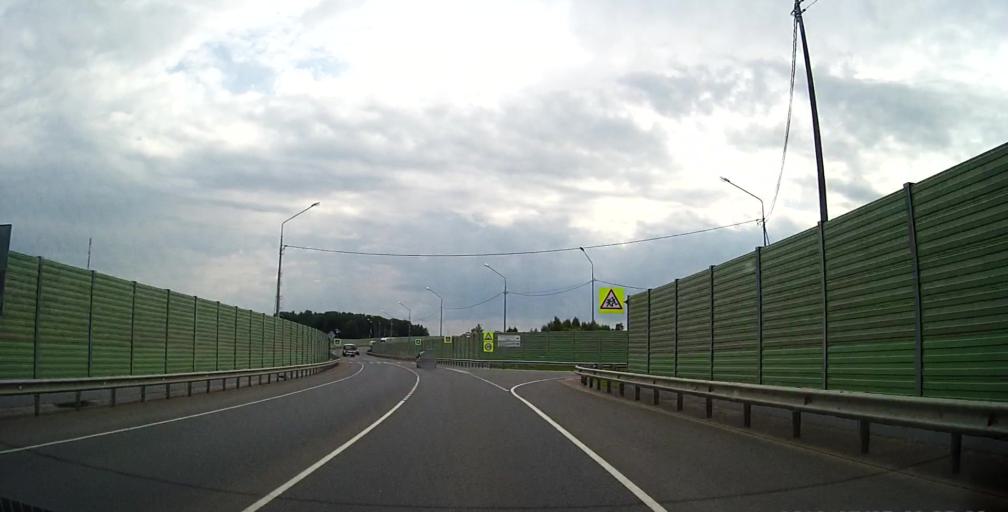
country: RU
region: Smolensk
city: Katyn'
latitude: 54.7692
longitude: 31.6935
